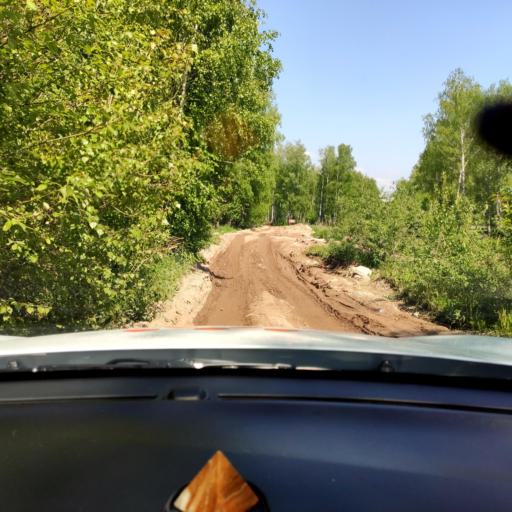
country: RU
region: Tatarstan
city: Stolbishchi
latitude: 55.7069
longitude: 49.1853
